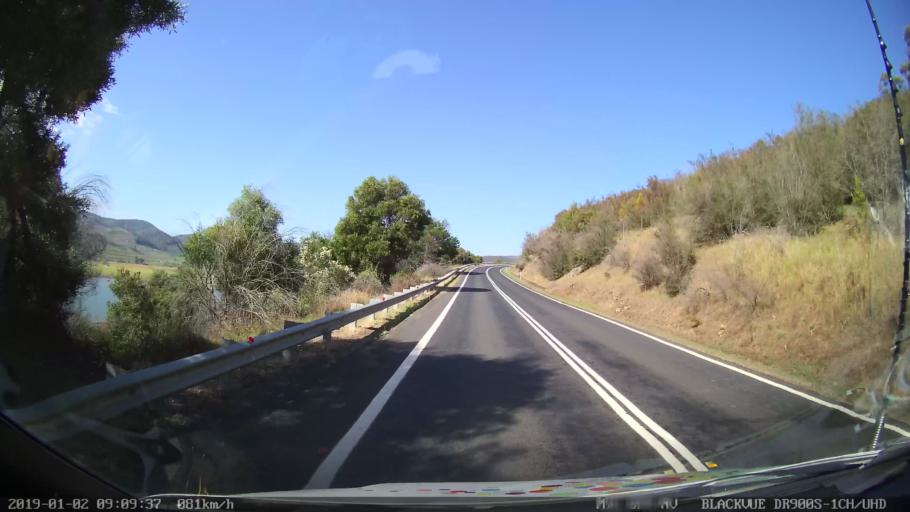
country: AU
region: New South Wales
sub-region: Tumut Shire
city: Tumut
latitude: -35.5255
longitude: 148.2772
